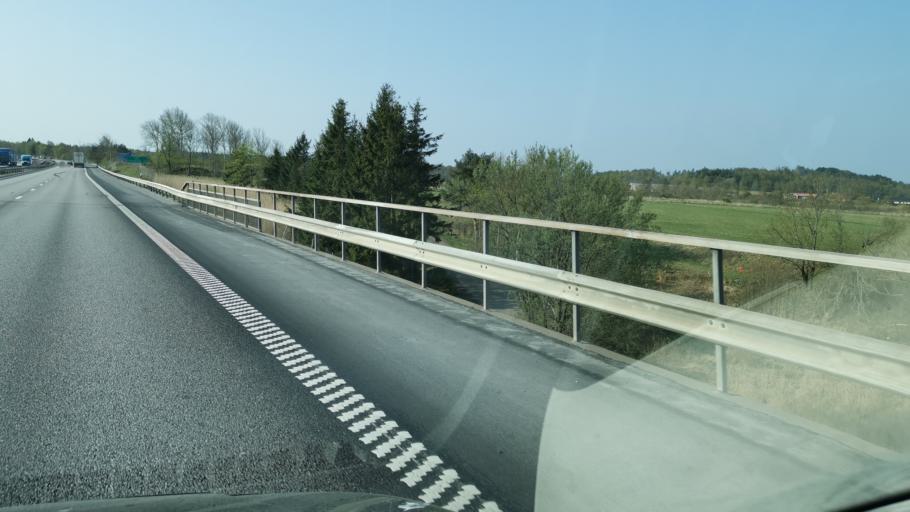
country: SE
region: Vaestra Goetaland
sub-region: Stenungsunds Kommun
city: Stora Hoga
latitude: 57.9780
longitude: 11.8405
